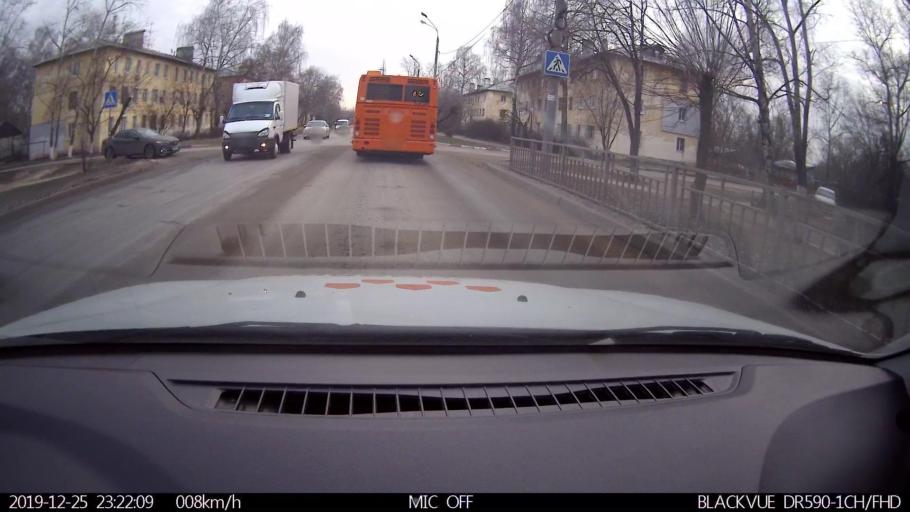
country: RU
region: Nizjnij Novgorod
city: Gorbatovka
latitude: 56.3526
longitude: 43.8337
